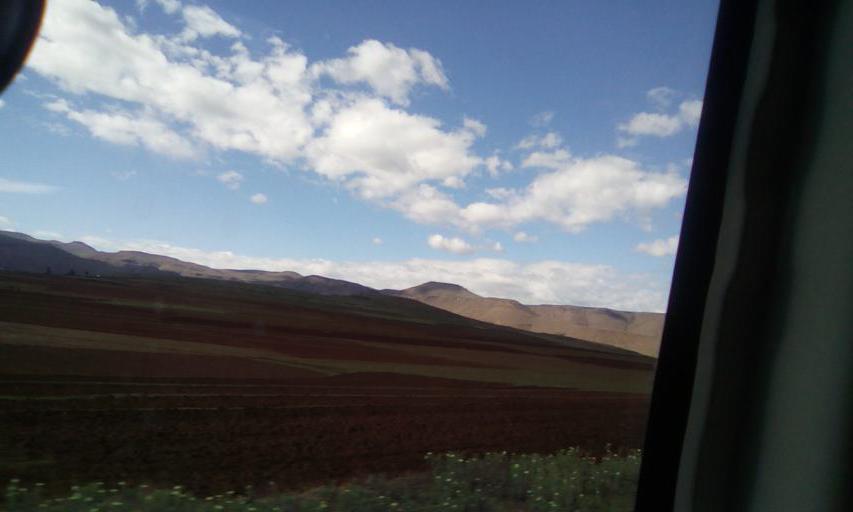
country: LS
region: Qacha's Nek
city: Qacha's Nek
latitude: -30.0220
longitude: 28.1983
